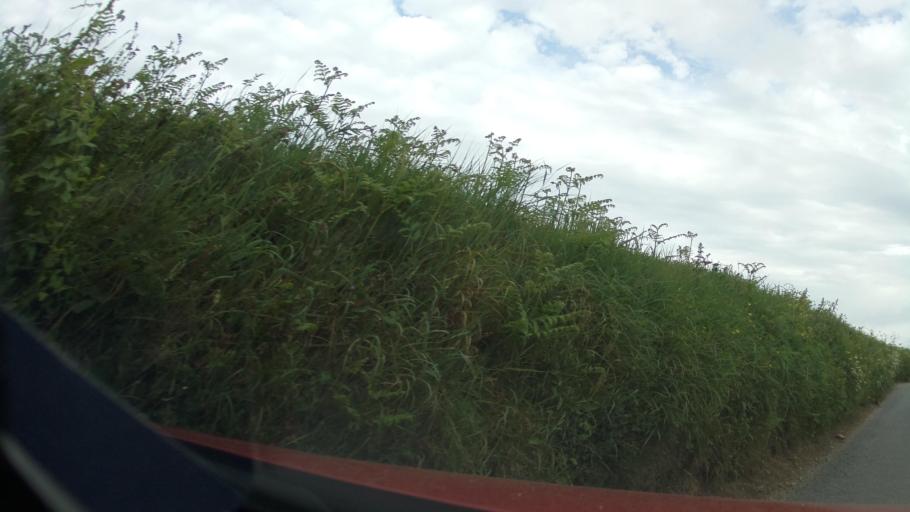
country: GB
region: England
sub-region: Devon
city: Dartmouth
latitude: 50.3362
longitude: -3.6498
